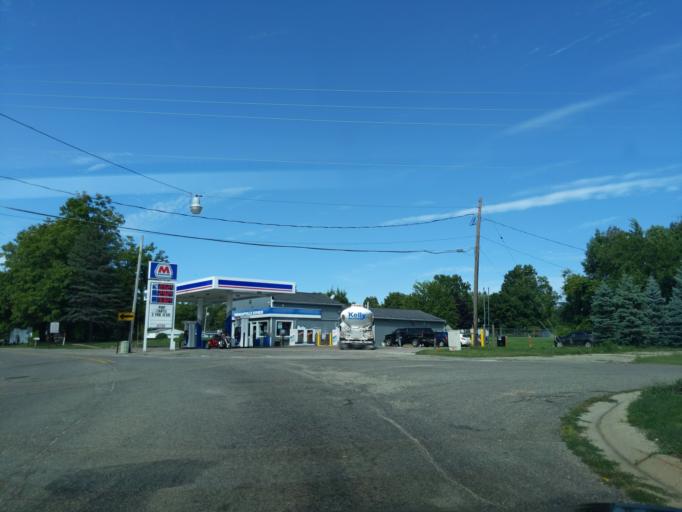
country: US
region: Michigan
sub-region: Barry County
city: Nashville
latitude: 42.6292
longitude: -85.0134
